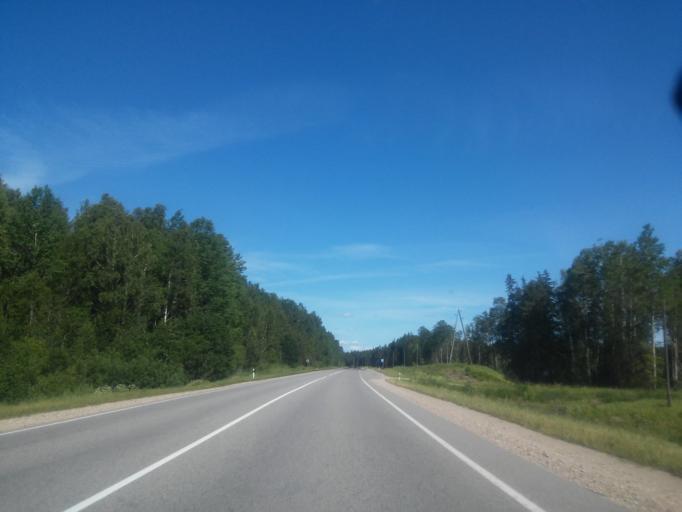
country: LV
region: Saldus Rajons
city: Saldus
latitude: 56.6746
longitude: 22.2632
